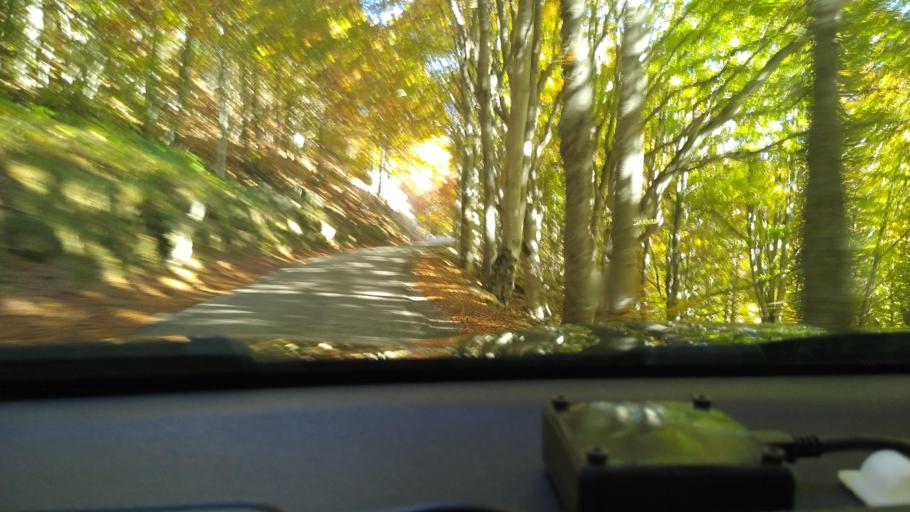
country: FR
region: Midi-Pyrenees
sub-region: Departement de l'Ariege
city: Ax-les-Thermes
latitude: 42.7296
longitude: 2.0158
